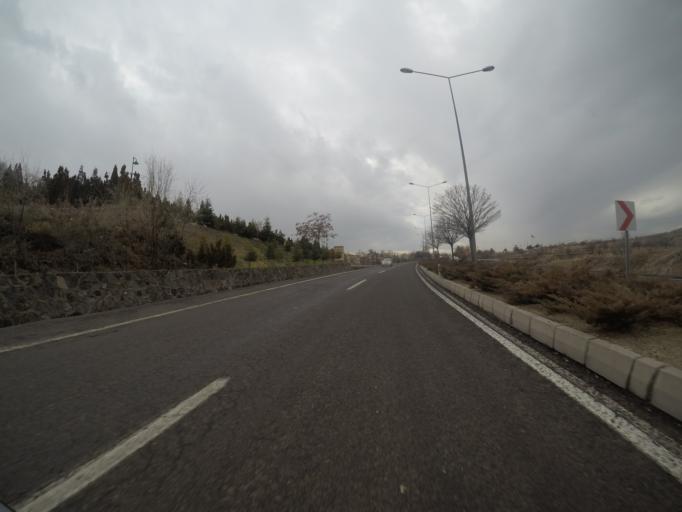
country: TR
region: Nevsehir
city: Urgub
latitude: 38.6363
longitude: 34.9009
